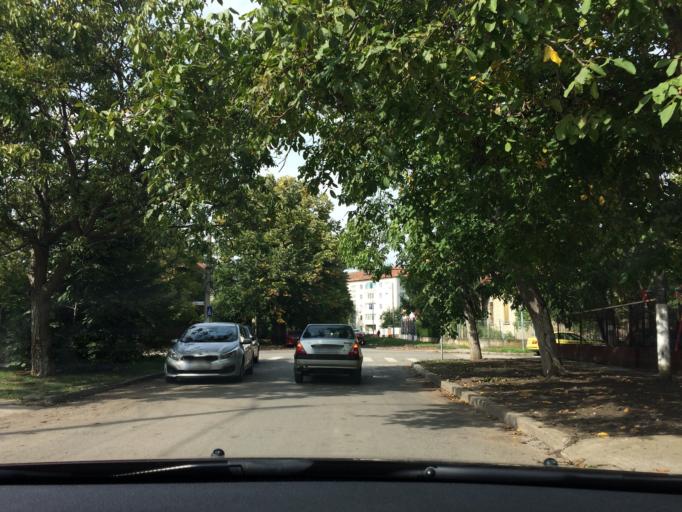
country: RO
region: Timis
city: Timisoara
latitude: 45.7594
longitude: 21.2132
